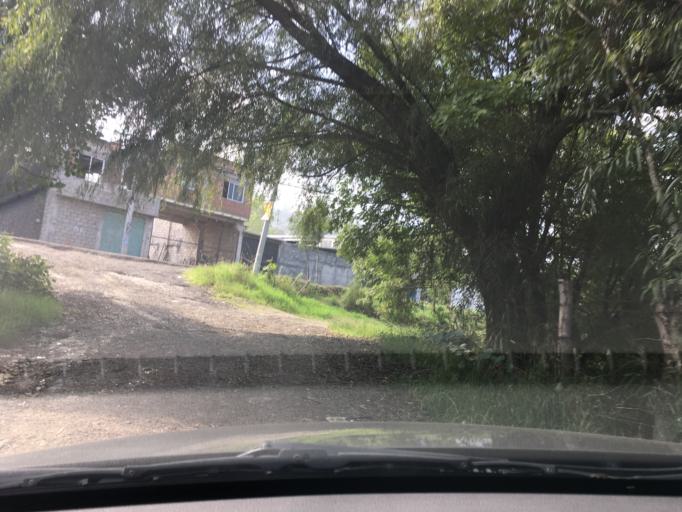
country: MX
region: Michoacan
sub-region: Morelia
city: Morelos
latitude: 19.6452
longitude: -101.2511
